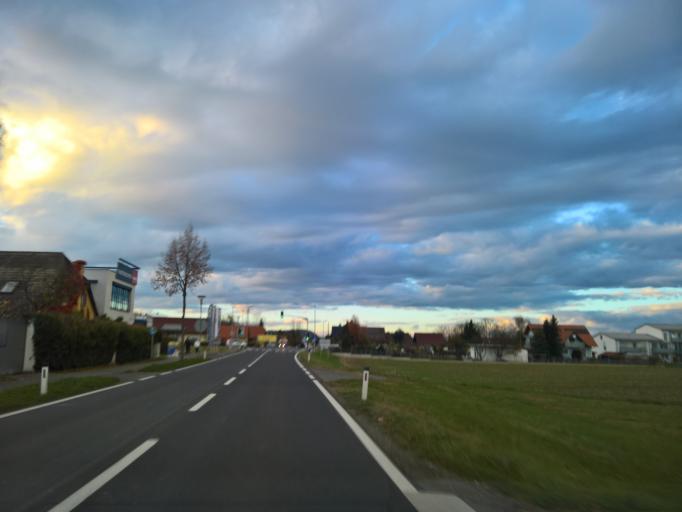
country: AT
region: Styria
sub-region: Politischer Bezirk Leibnitz
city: Kaindorf an der Sulm
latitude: 46.8125
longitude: 15.5493
